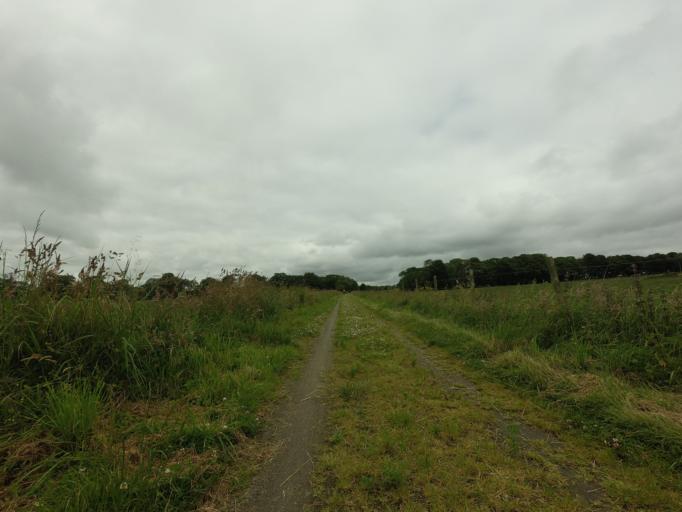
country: GB
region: Scotland
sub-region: Aberdeenshire
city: Ellon
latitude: 57.4856
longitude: -2.1351
